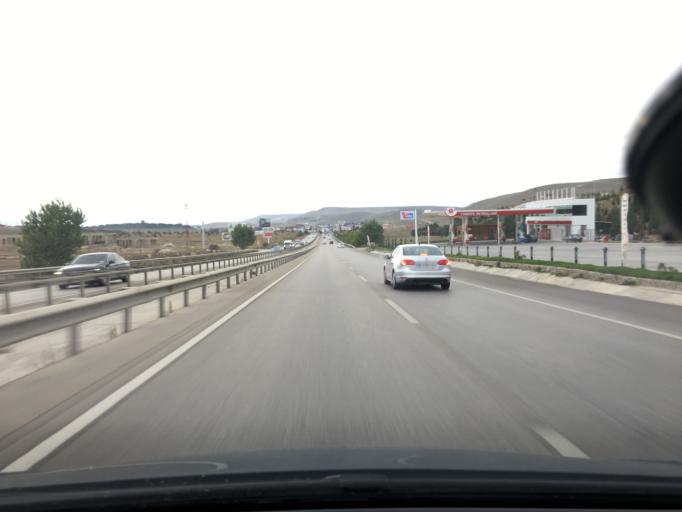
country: TR
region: Afyonkarahisar
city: Afyonkarahisar
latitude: 38.7926
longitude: 30.4127
